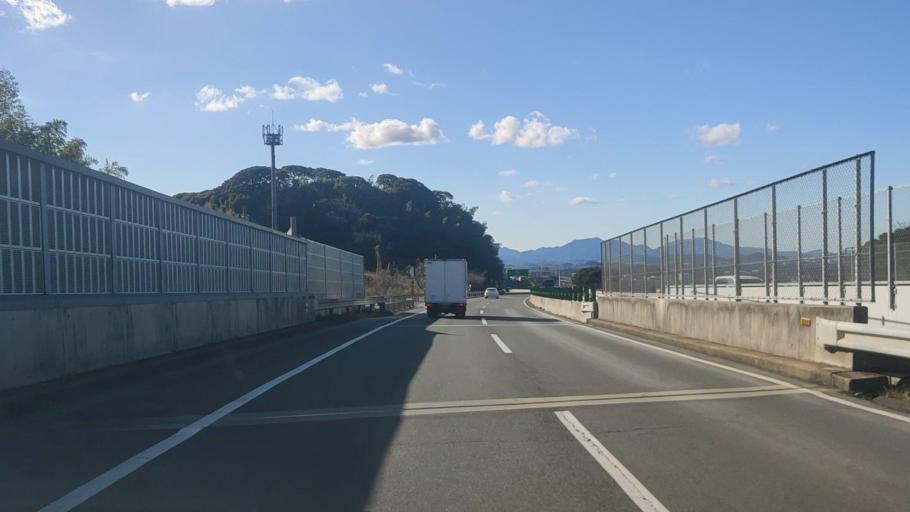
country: JP
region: Fukuoka
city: Kitakyushu
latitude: 33.8511
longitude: 130.7746
